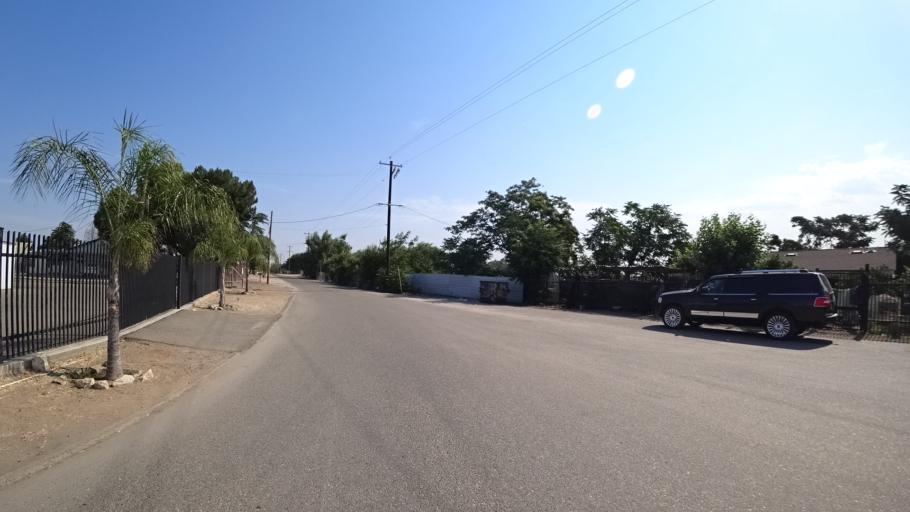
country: US
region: California
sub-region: Fresno County
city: West Park
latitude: 36.7389
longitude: -119.8535
